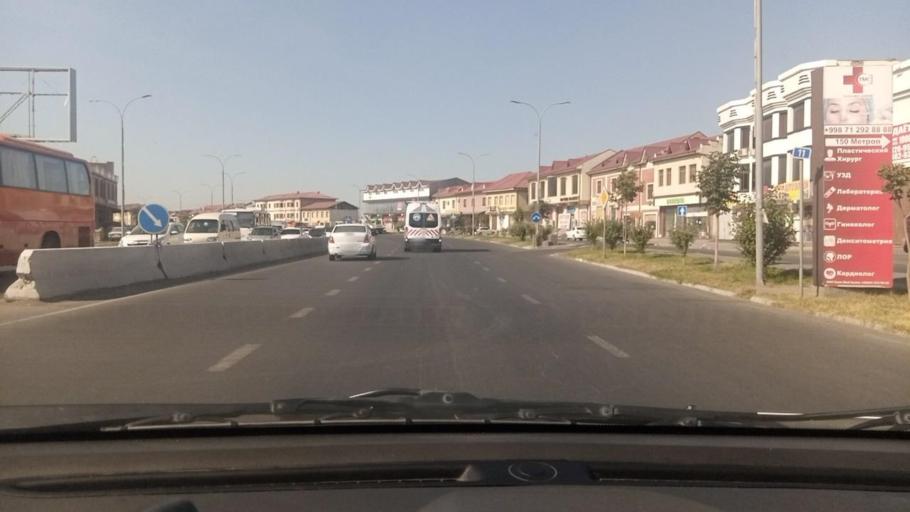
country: UZ
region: Toshkent Shahri
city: Bektemir
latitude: 41.2247
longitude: 69.3347
